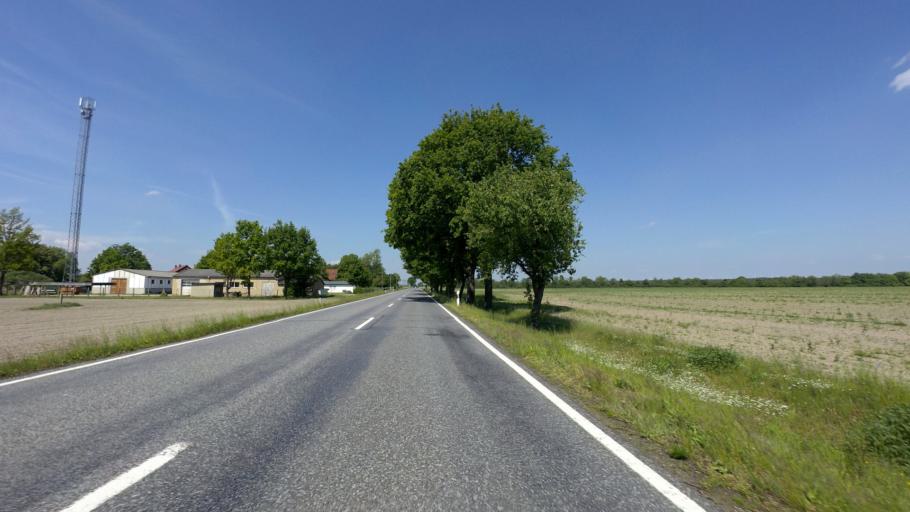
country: DE
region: Brandenburg
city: Luckau
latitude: 51.8221
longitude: 13.7954
